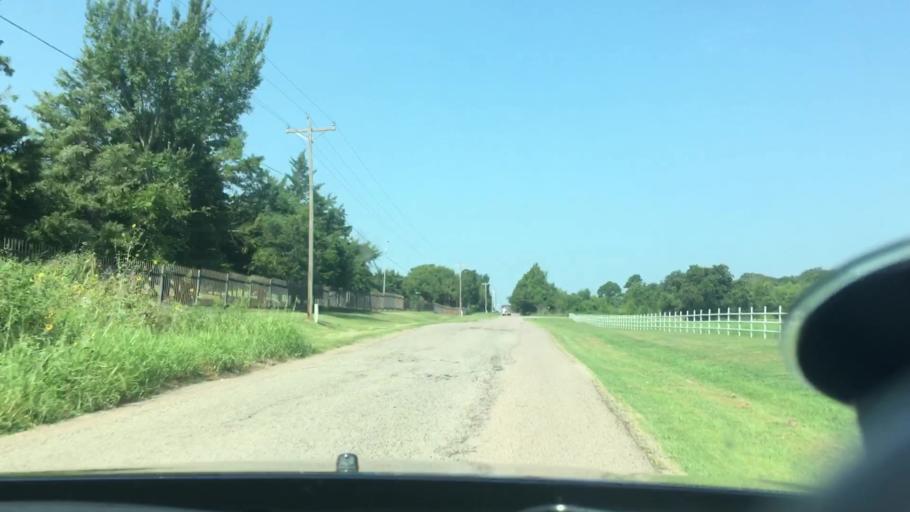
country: US
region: Oklahoma
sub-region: Bryan County
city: Durant
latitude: 34.0267
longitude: -96.4055
